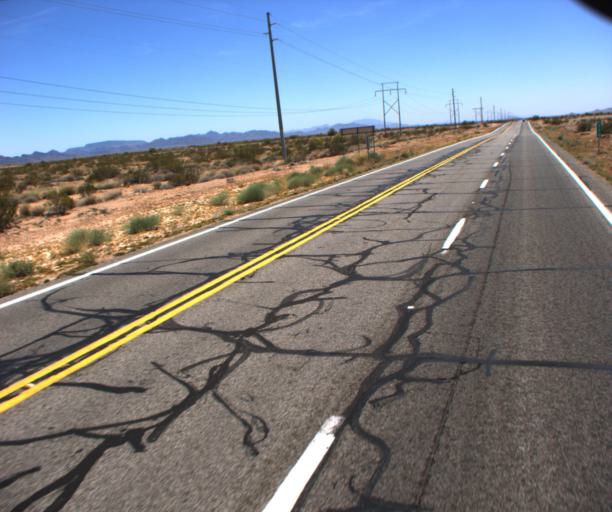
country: US
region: Arizona
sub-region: La Paz County
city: Quartzsite
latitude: 33.8119
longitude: -114.2171
